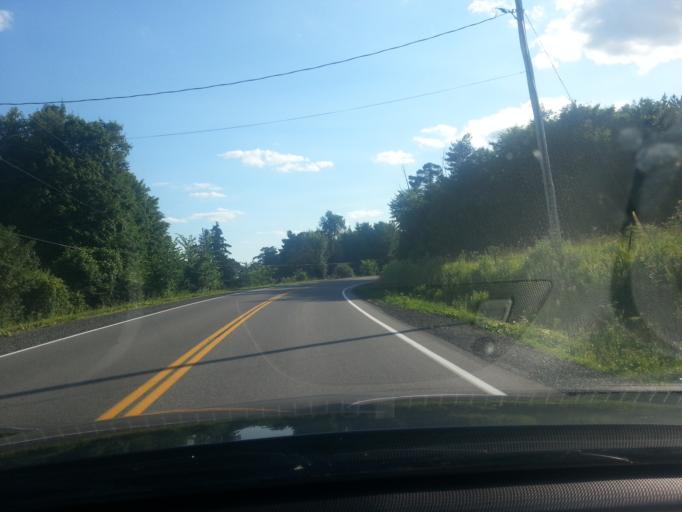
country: CA
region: Ontario
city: Carleton Place
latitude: 45.0716
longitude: -76.3064
